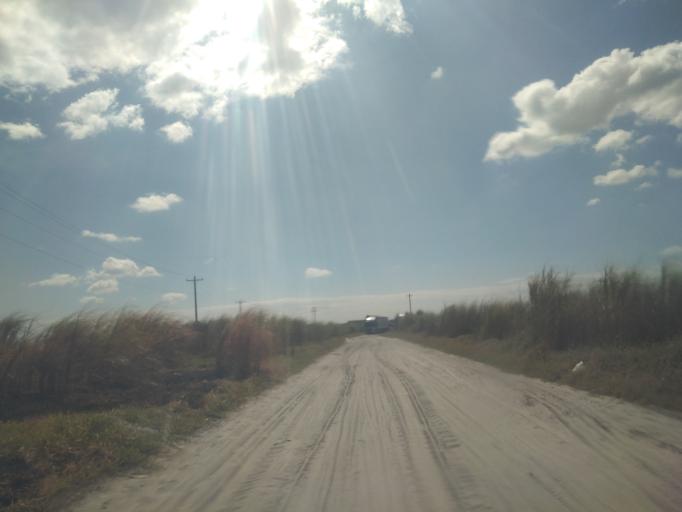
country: PH
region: Central Luzon
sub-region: Province of Pampanga
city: Balas
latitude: 15.0611
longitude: 120.5948
